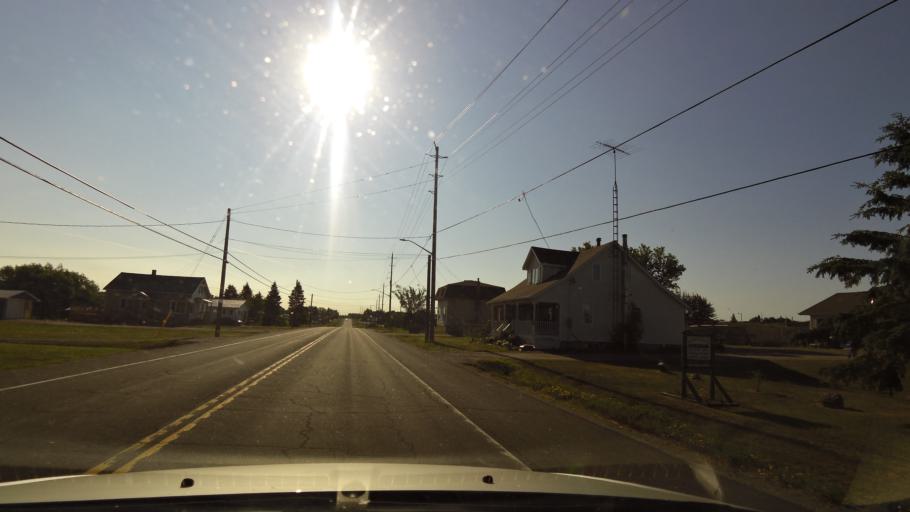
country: CA
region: Ontario
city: Greater Sudbury
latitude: 46.1047
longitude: -80.6171
